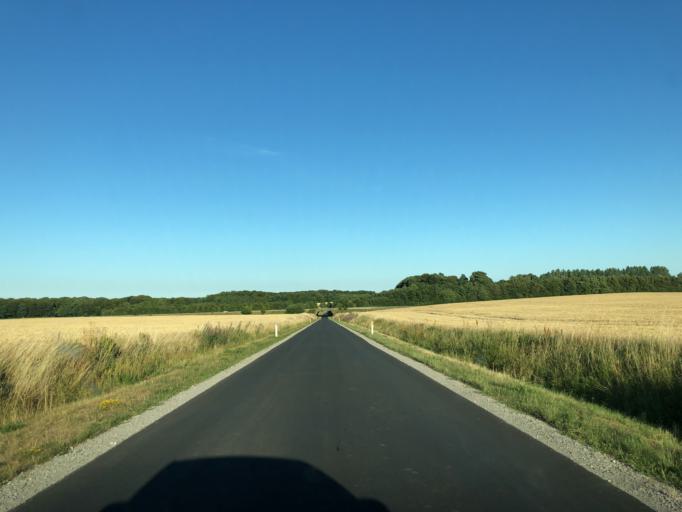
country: DK
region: Central Jutland
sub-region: Horsens Kommune
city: Horsens
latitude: 55.9603
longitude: 9.8332
